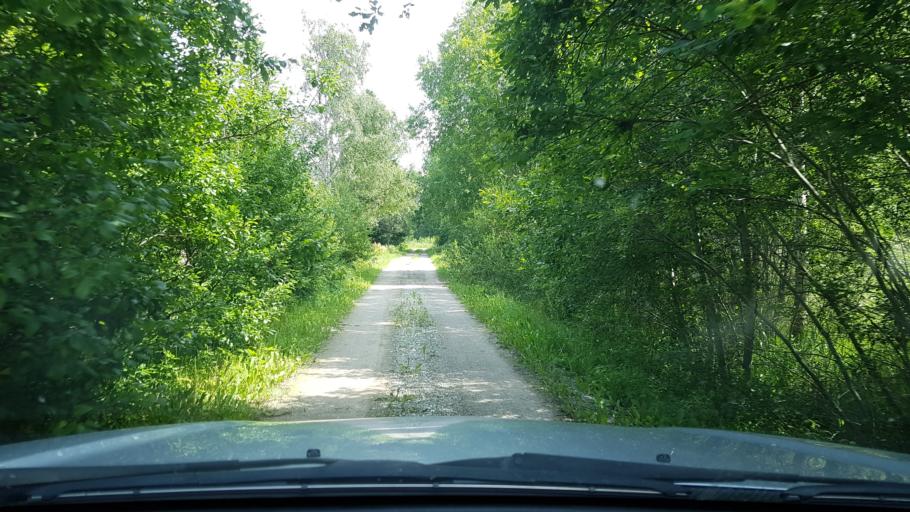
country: EE
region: Ida-Virumaa
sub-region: Sillamaee linn
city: Sillamae
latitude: 59.3632
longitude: 27.8932
